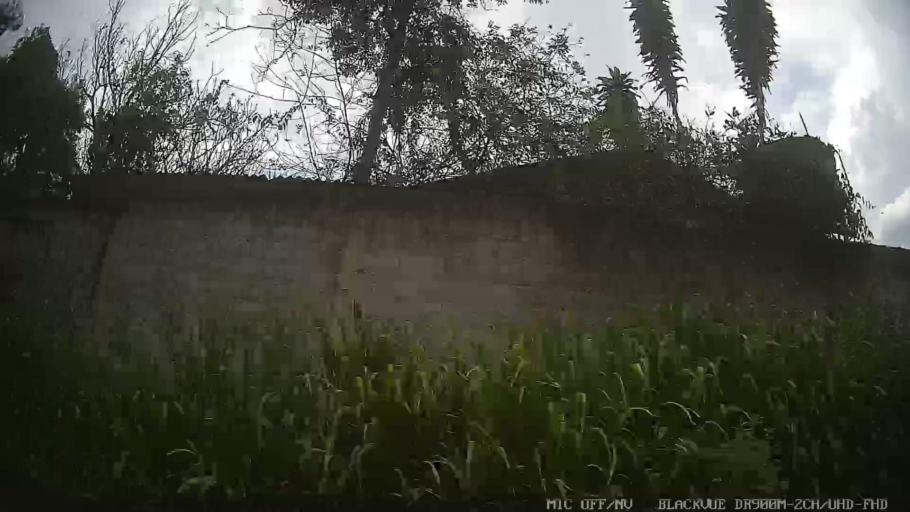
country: BR
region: Sao Paulo
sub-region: Aruja
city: Aruja
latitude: -23.4286
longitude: -46.2325
